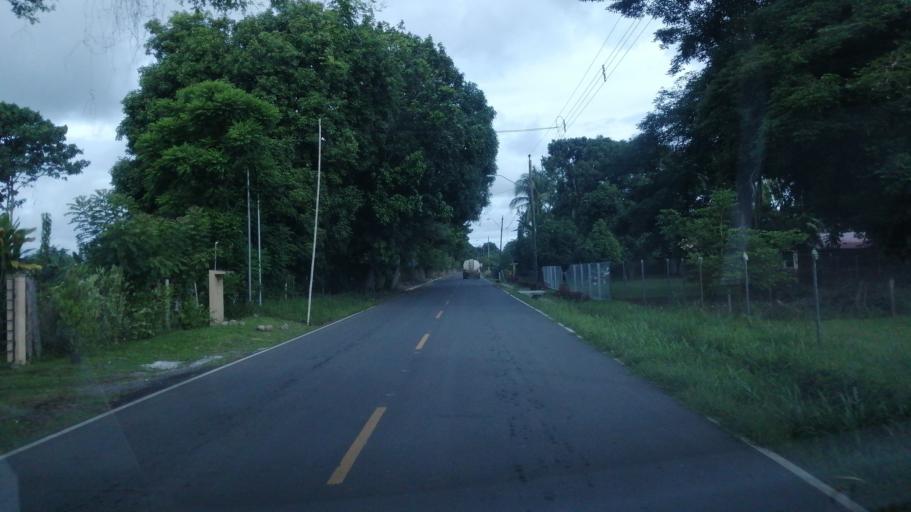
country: PA
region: Chiriqui
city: Alanje
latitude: 8.4161
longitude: -82.5192
